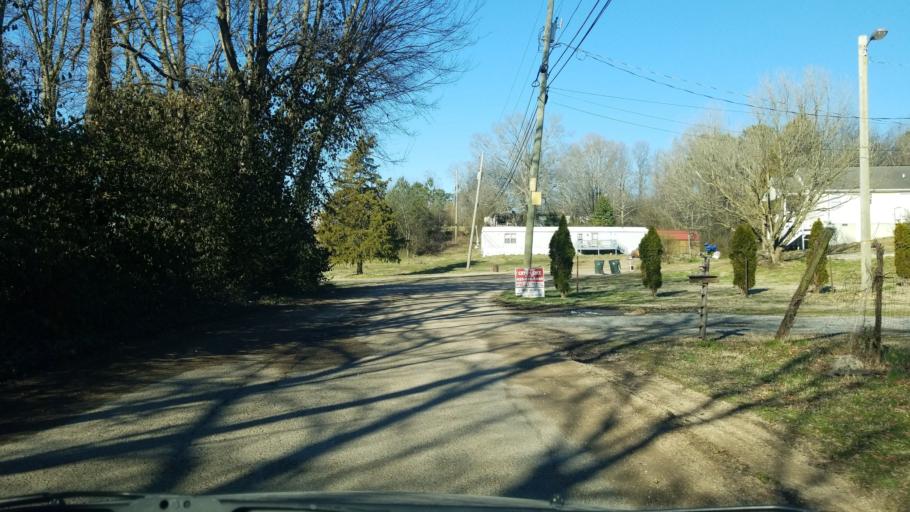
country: US
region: Tennessee
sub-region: Hamilton County
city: Collegedale
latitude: 35.0705
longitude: -85.1001
